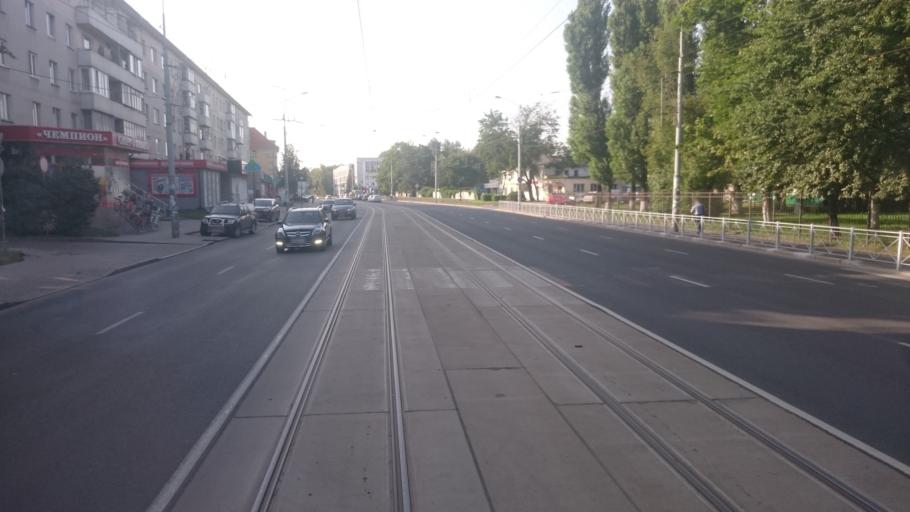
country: RU
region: Kaliningrad
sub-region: Gorod Kaliningrad
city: Kaliningrad
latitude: 54.7287
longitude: 20.4923
